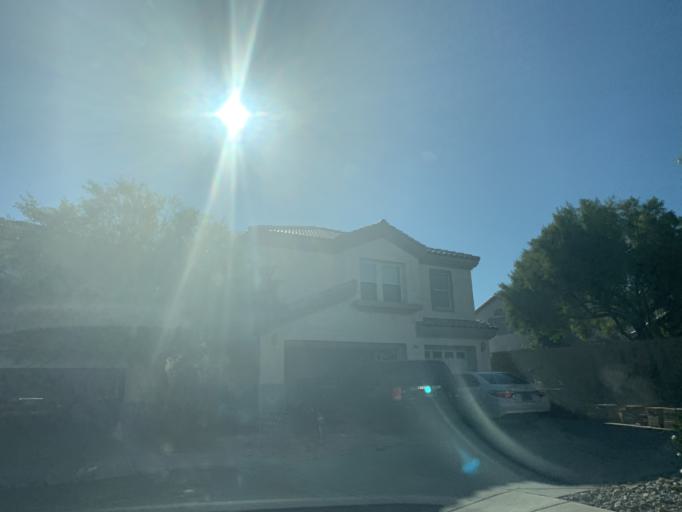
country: US
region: Nevada
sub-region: Clark County
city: Summerlin South
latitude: 36.1257
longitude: -115.3071
